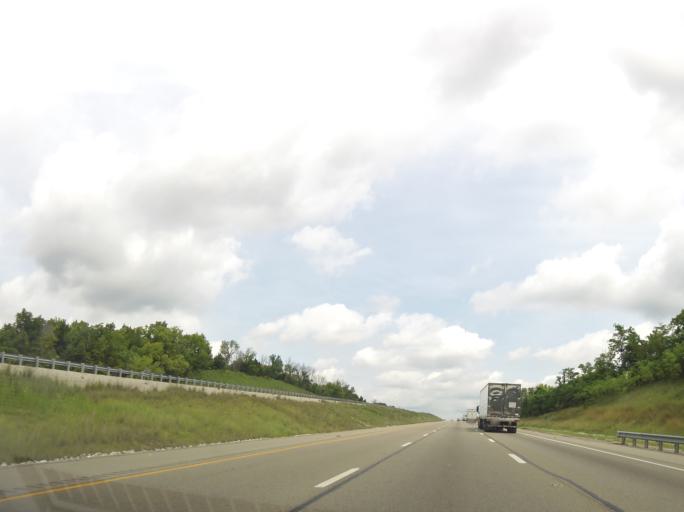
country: US
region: Kentucky
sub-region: Grant County
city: Williamstown
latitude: 38.5155
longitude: -84.5881
